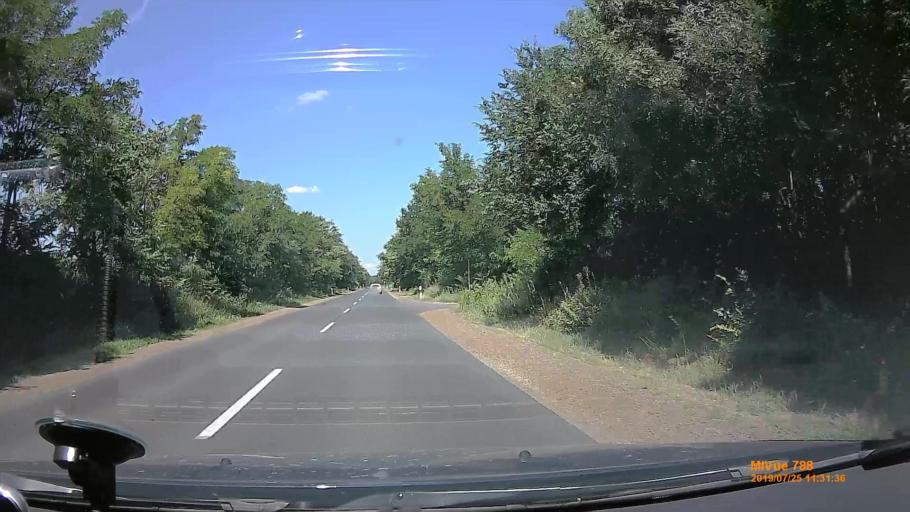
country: HU
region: Szabolcs-Szatmar-Bereg
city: Nagykallo
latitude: 47.9084
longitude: 21.7817
